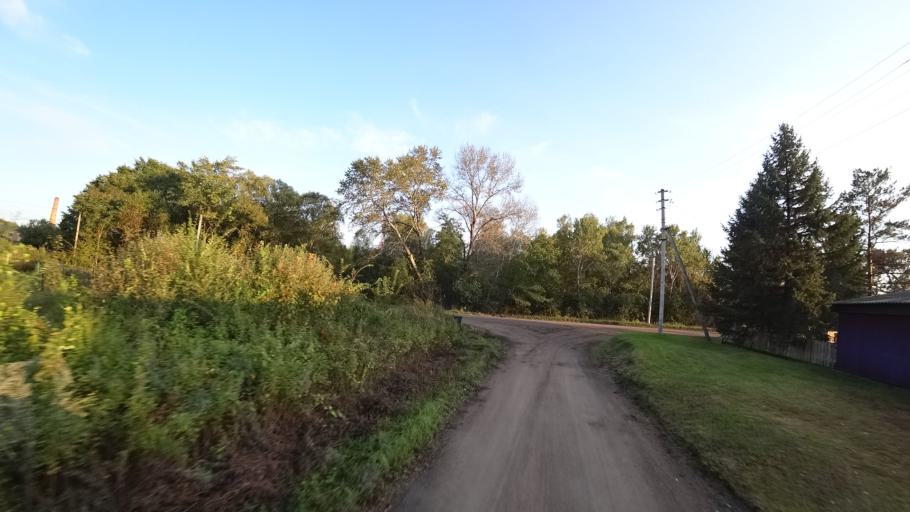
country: RU
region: Amur
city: Arkhara
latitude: 49.3627
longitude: 130.1173
